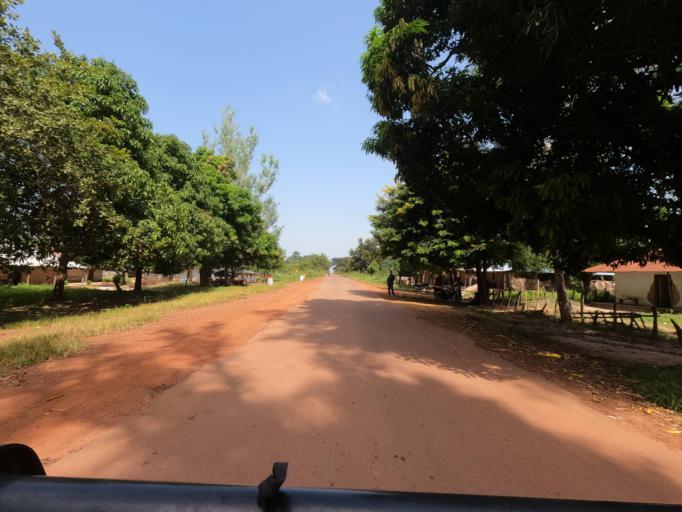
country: GW
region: Oio
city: Bissora
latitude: 12.3357
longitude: -15.7610
